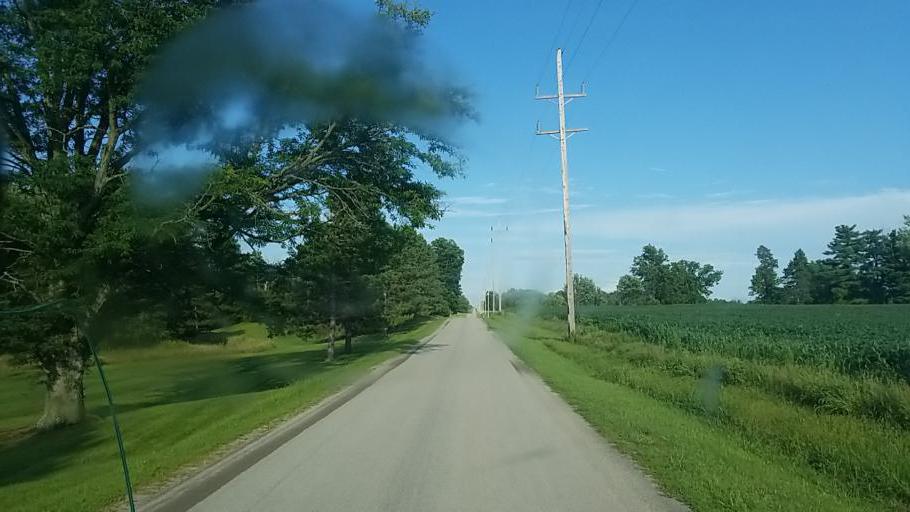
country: US
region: Ohio
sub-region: Wyandot County
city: Upper Sandusky
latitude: 40.8147
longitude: -83.2048
